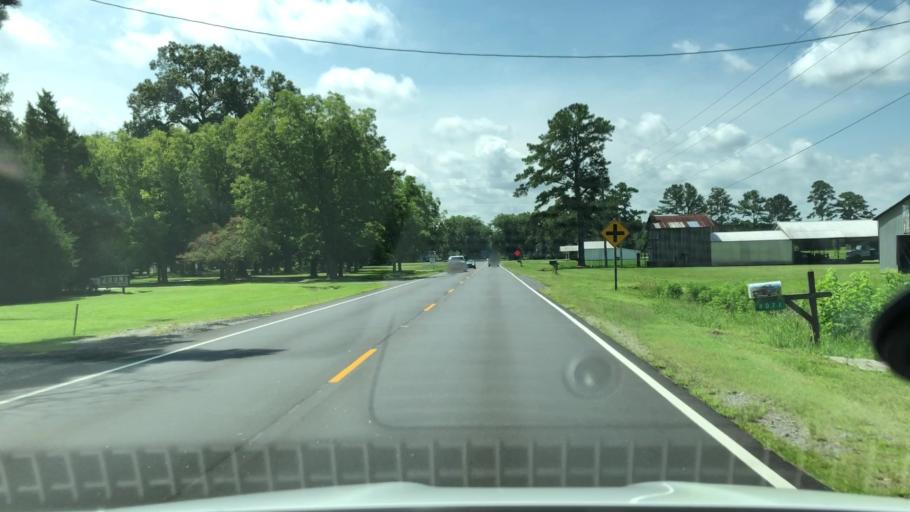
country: US
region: North Carolina
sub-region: Martin County
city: Williamston
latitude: 35.7436
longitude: -77.0758
